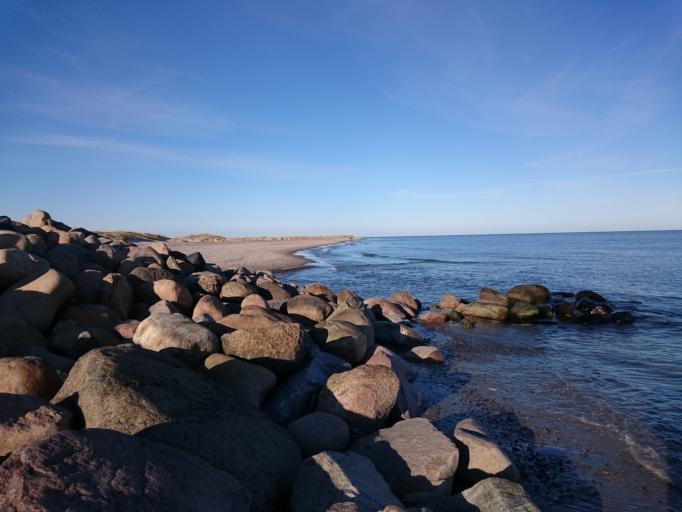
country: DK
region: North Denmark
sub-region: Frederikshavn Kommune
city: Skagen
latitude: 57.7400
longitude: 10.6391
